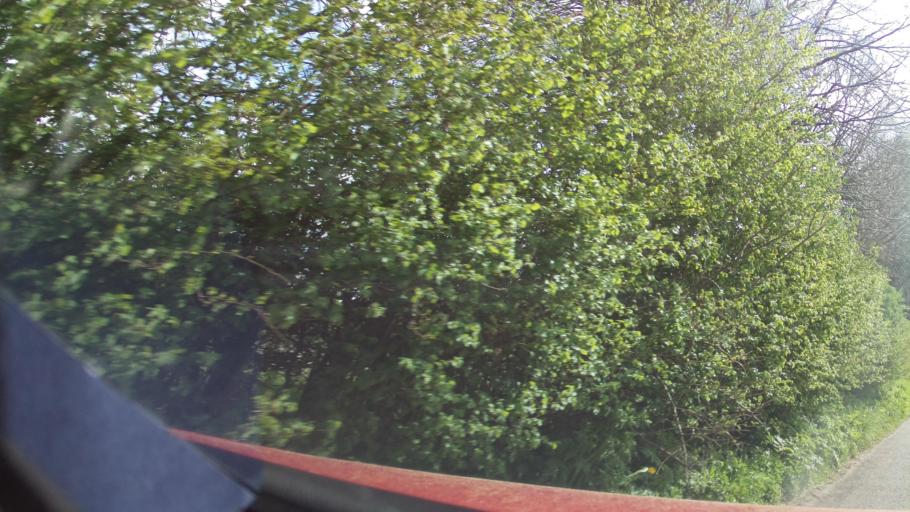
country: GB
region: England
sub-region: Hampshire
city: Abbotts Ann
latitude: 51.1036
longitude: -1.5069
